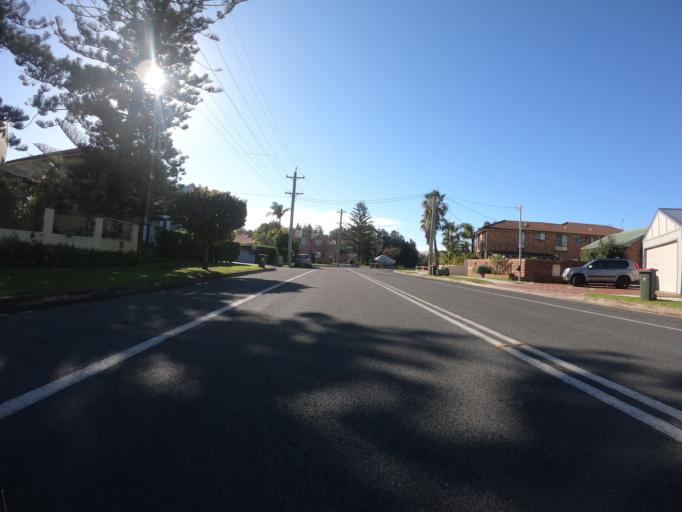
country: AU
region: New South Wales
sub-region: Wollongong
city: East Corrimal
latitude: -34.3808
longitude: 150.9131
